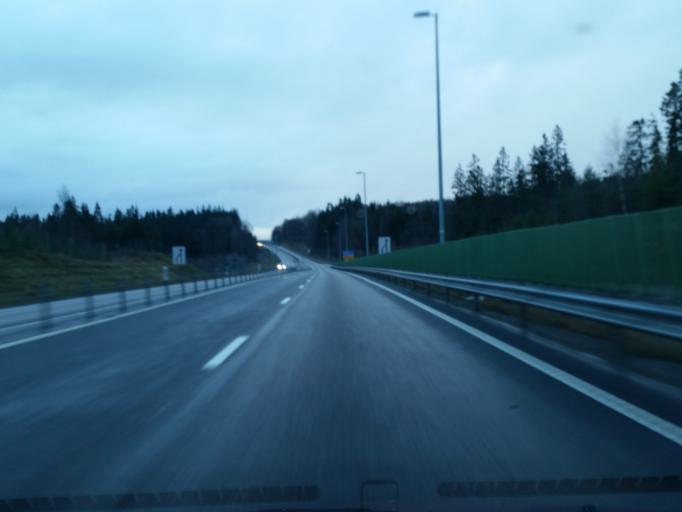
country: SE
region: Vaestra Goetaland
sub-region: Boras Kommun
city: Ganghester
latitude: 57.6737
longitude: 12.9967
